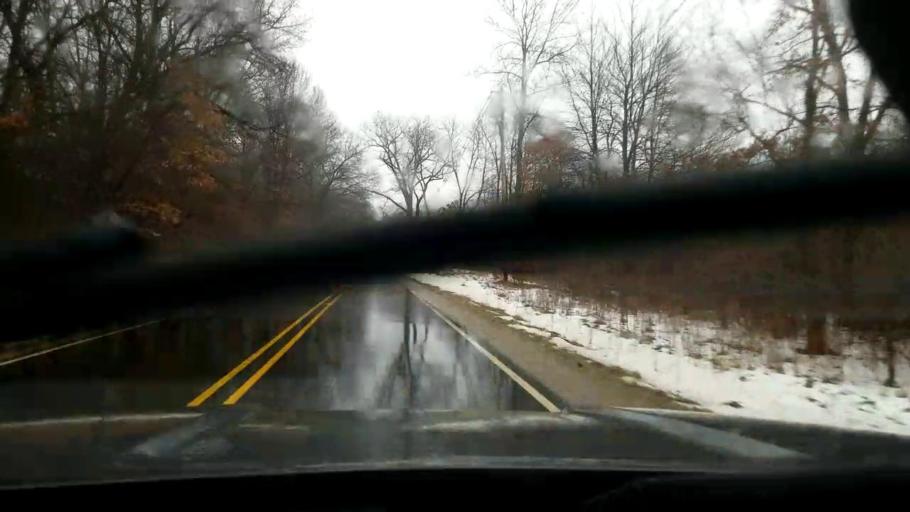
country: US
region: Michigan
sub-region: Jackson County
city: Grass Lake
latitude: 42.3244
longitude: -84.2189
